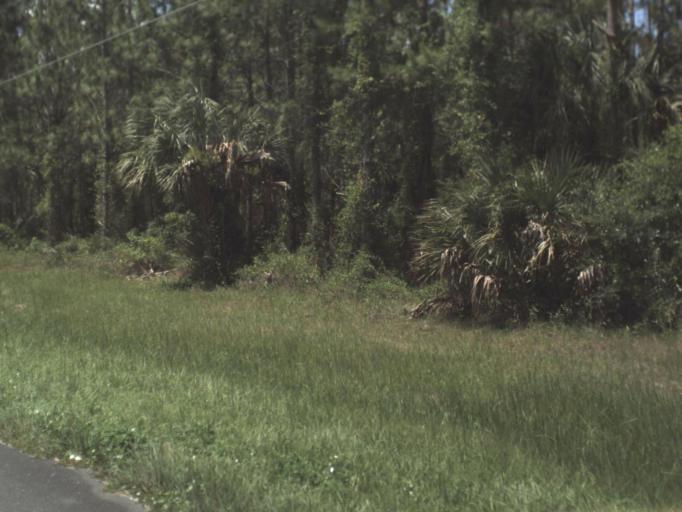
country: US
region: Florida
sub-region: Alachua County
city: Hawthorne
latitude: 29.6189
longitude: -82.0267
